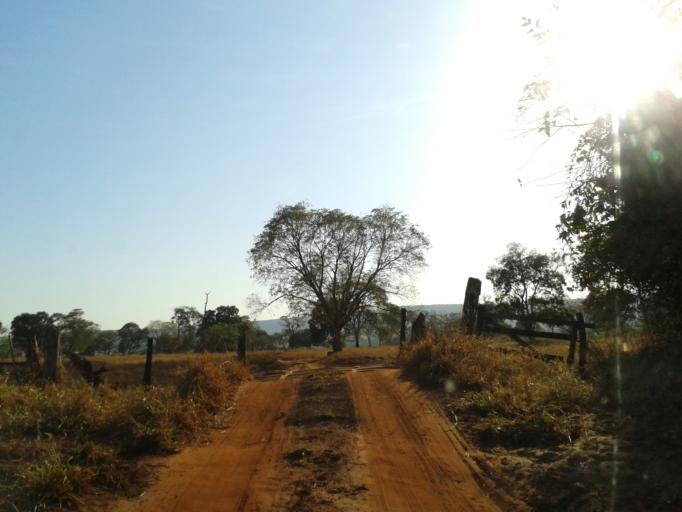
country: BR
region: Minas Gerais
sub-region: Santa Vitoria
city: Santa Vitoria
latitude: -19.1781
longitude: -50.0241
